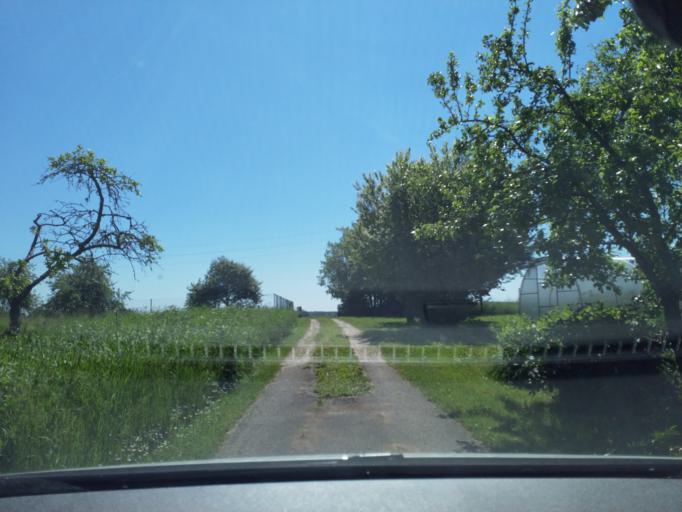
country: LV
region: Kuldigas Rajons
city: Kuldiga
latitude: 56.9590
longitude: 21.9540
